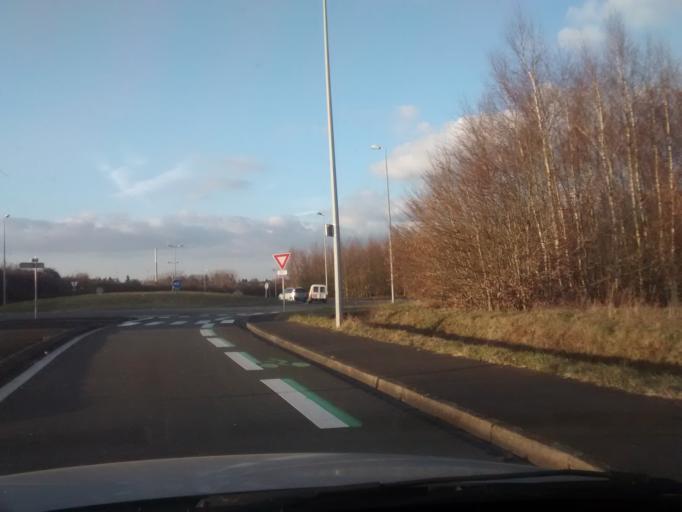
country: FR
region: Pays de la Loire
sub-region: Departement de la Sarthe
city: Sarge-les-le-Mans
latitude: 48.0155
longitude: 0.2391
